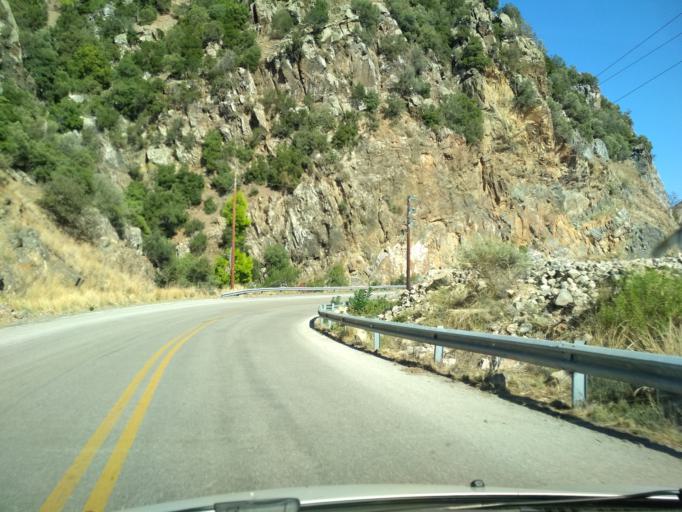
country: GR
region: Central Greece
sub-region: Nomos Evvoias
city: Roviai
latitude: 38.8480
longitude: 23.1561
